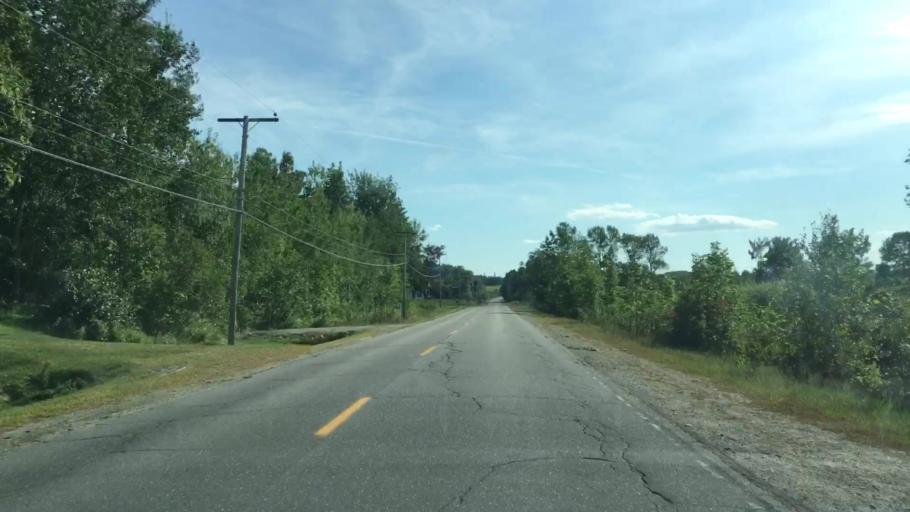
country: US
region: Maine
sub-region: Penobscot County
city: Lincoln
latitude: 45.3275
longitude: -68.5316
